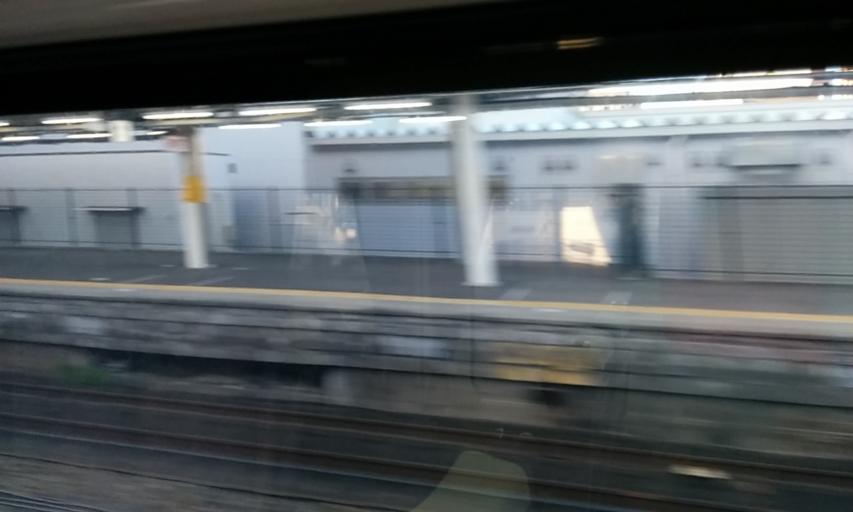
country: JP
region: Aichi
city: Kasugai
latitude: 35.2433
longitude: 136.9855
